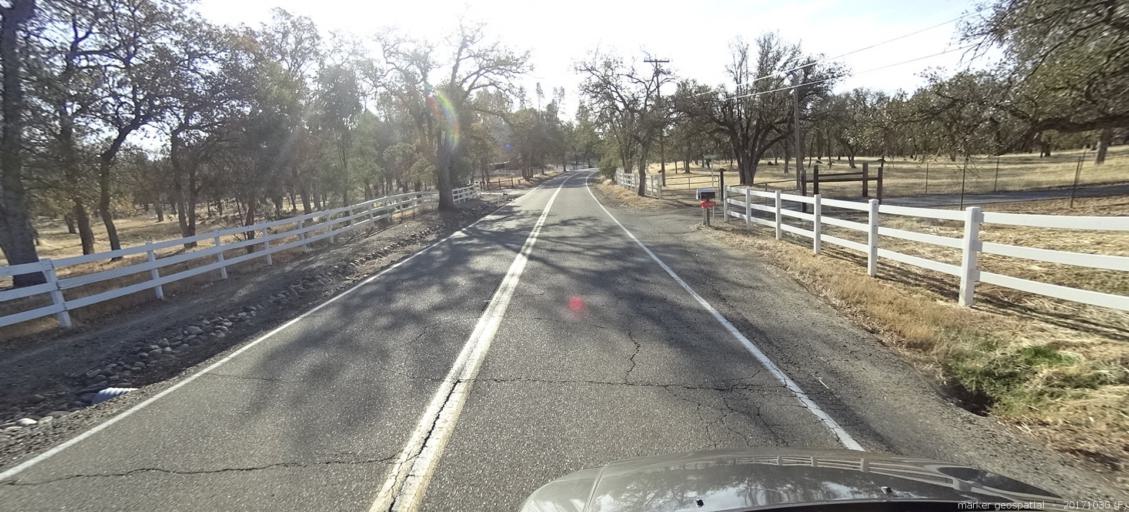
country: US
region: California
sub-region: Shasta County
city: Palo Cedro
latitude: 40.5622
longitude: -122.1898
